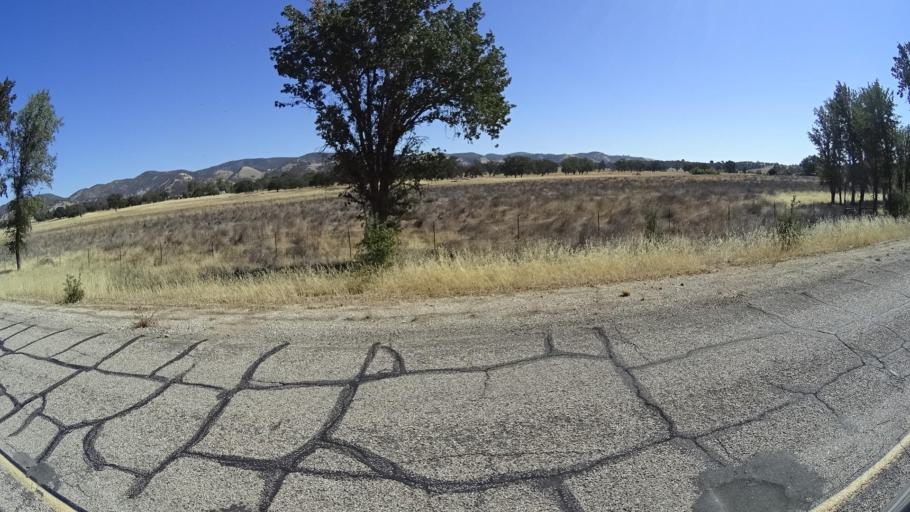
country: US
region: California
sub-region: Monterey County
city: King City
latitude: 36.0231
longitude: -121.1783
